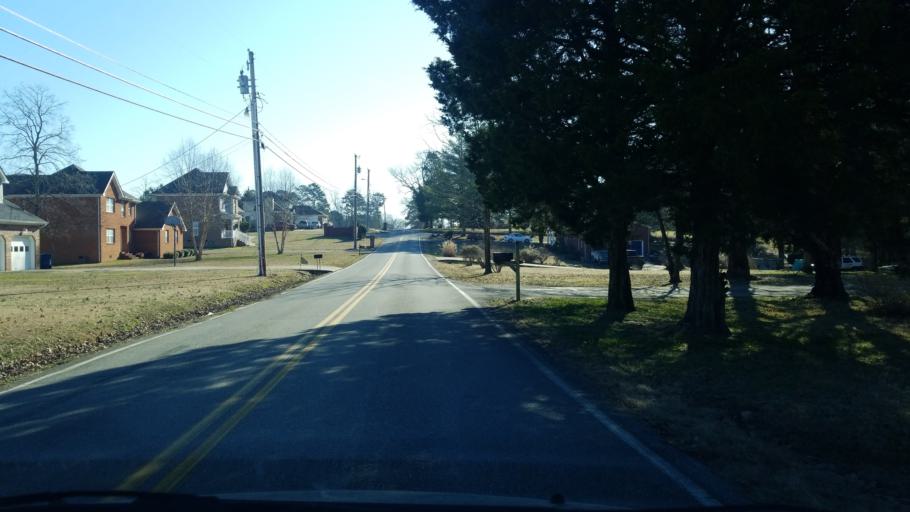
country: US
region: Tennessee
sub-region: Hamilton County
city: Collegedale
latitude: 35.0640
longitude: -85.1057
